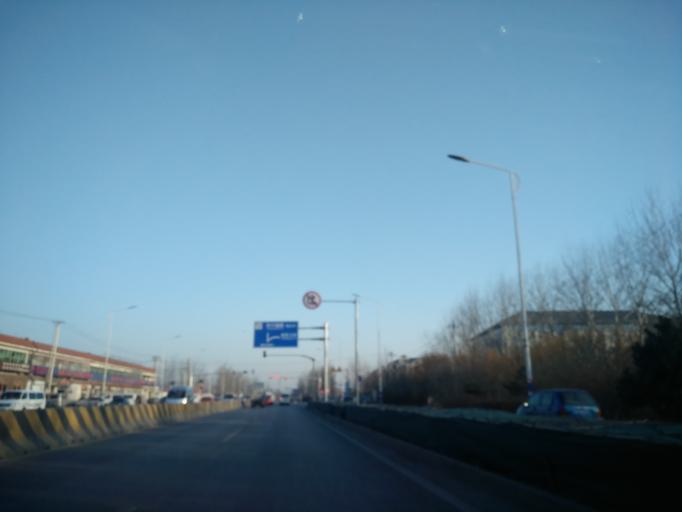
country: CN
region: Beijing
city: Weishanzhuang
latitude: 39.6654
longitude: 116.4081
